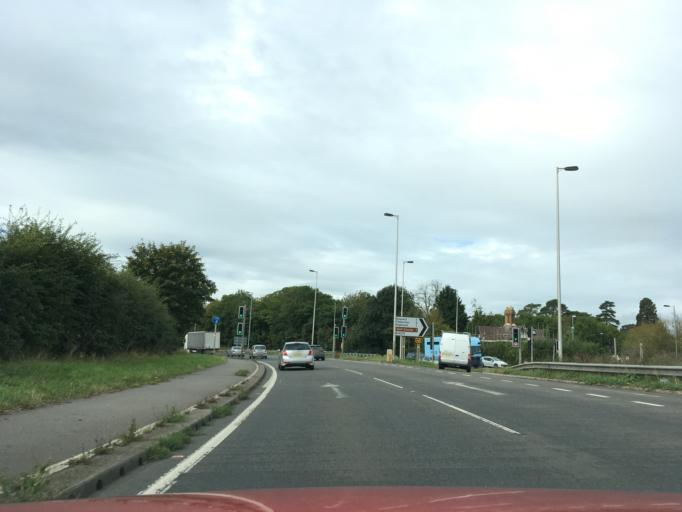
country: GB
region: England
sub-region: Gloucestershire
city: Gloucester
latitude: 51.8726
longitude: -2.2886
